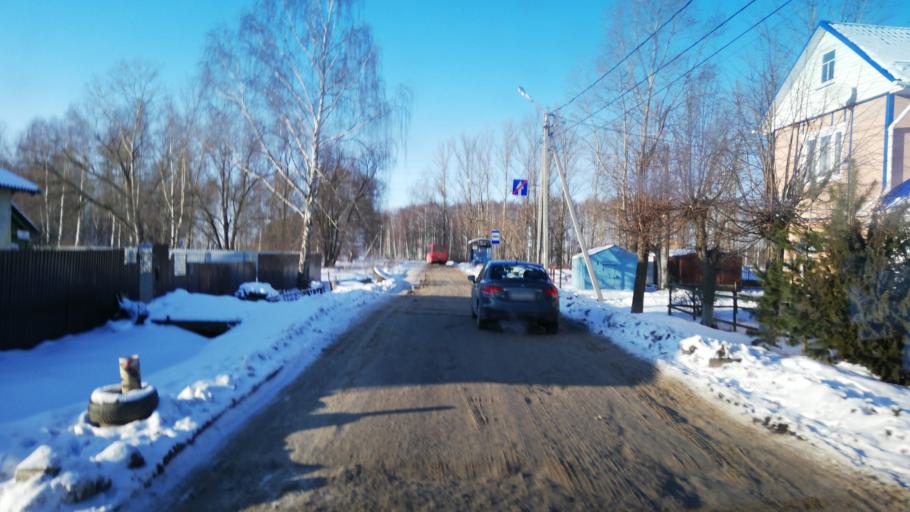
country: RU
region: Jaroslavl
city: Yaroslavl
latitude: 57.6194
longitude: 39.8138
